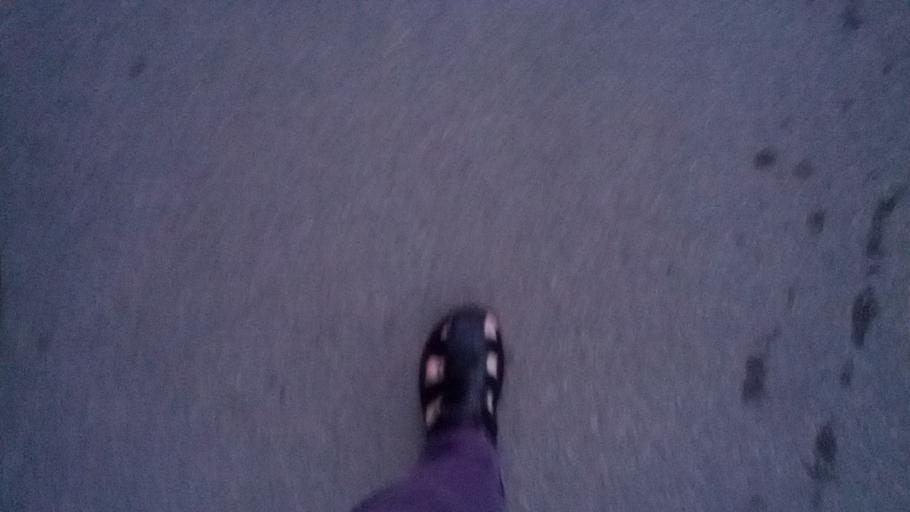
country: RU
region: St.-Petersburg
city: Obukhovo
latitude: 59.9045
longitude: 30.4638
